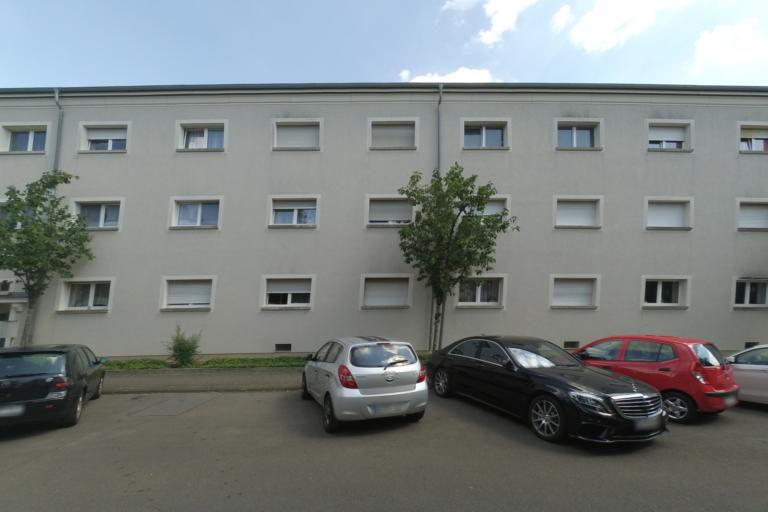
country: DE
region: Rheinland-Pfalz
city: Ludwigshafen am Rhein
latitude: 49.4926
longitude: 8.4189
